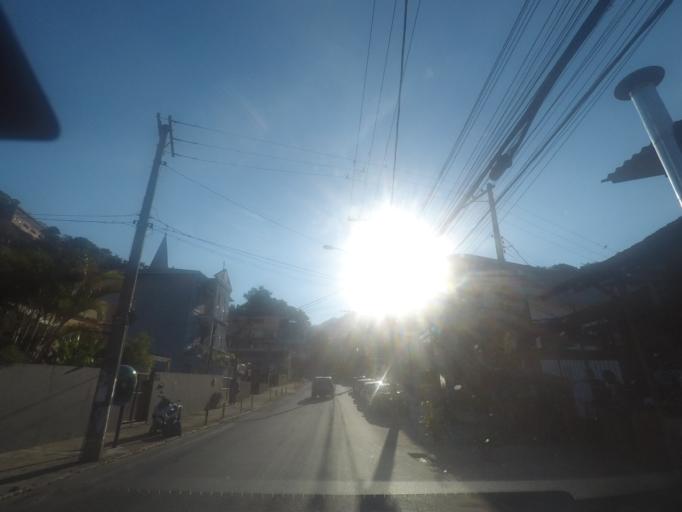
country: BR
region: Rio de Janeiro
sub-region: Petropolis
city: Petropolis
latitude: -22.4895
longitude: -43.1541
